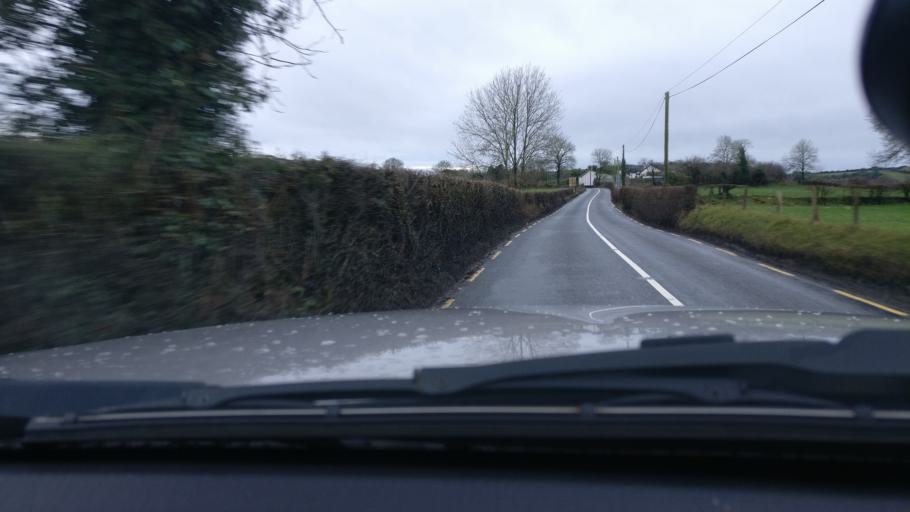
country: IE
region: Leinster
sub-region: An Longfort
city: Granard
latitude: 53.8105
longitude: -7.3743
